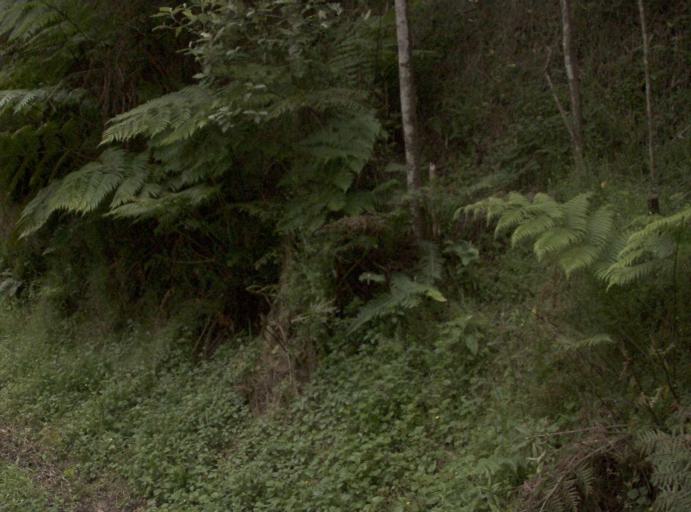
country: AU
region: Victoria
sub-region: Latrobe
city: Traralgon
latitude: -38.4570
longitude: 146.5454
